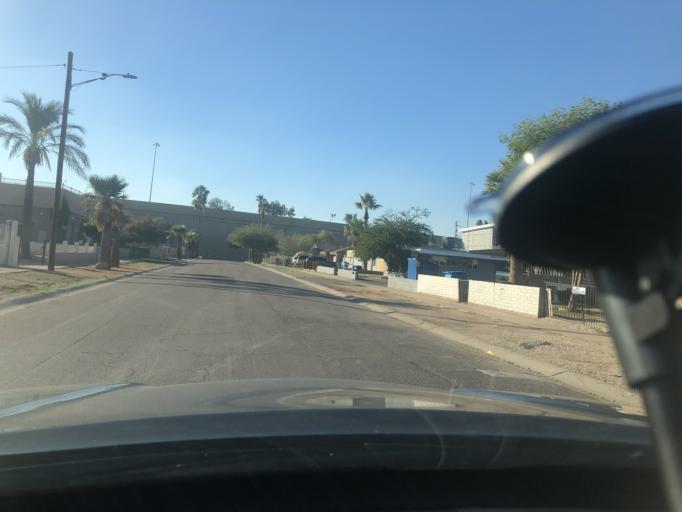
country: US
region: Arizona
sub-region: Maricopa County
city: Phoenix
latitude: 33.4540
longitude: -112.0343
